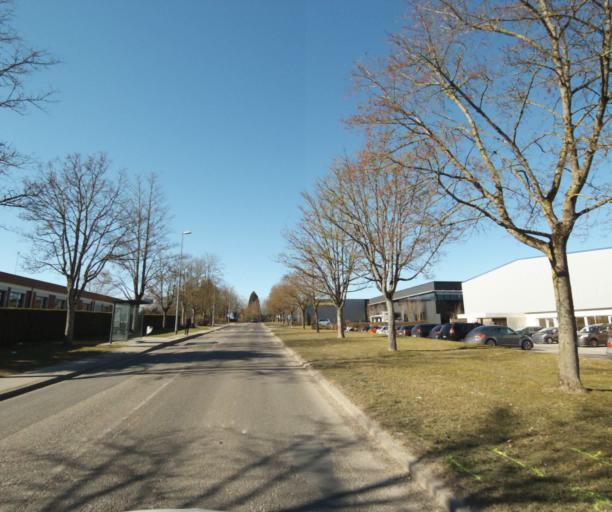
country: FR
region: Lorraine
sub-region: Departement de Meurthe-et-Moselle
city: Richardmenil
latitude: 48.6126
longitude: 6.1853
